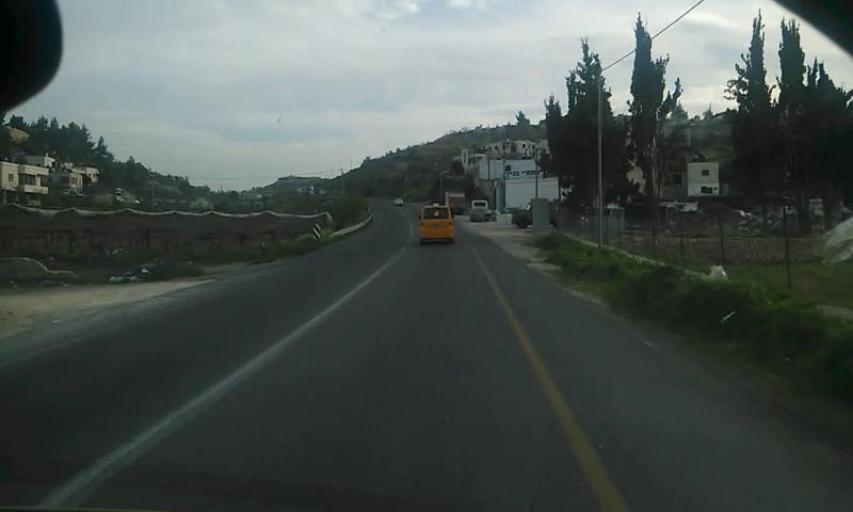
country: PS
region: West Bank
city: Bayt Ummar
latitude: 31.6121
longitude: 35.1134
